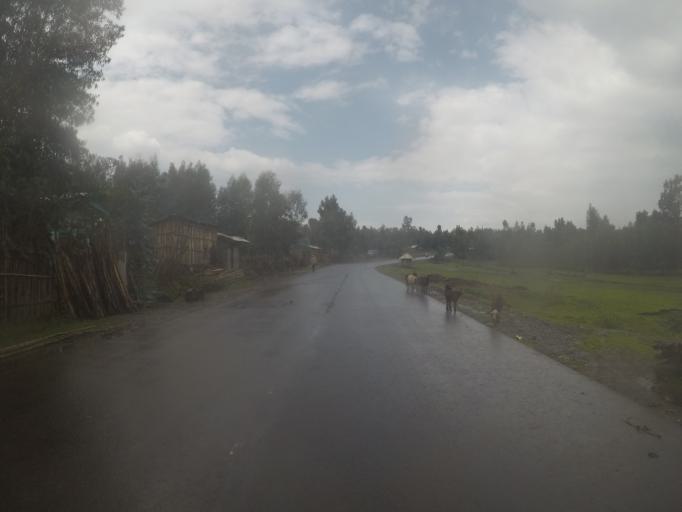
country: ET
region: Amhara
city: Debark'
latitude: 13.1027
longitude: 37.8522
